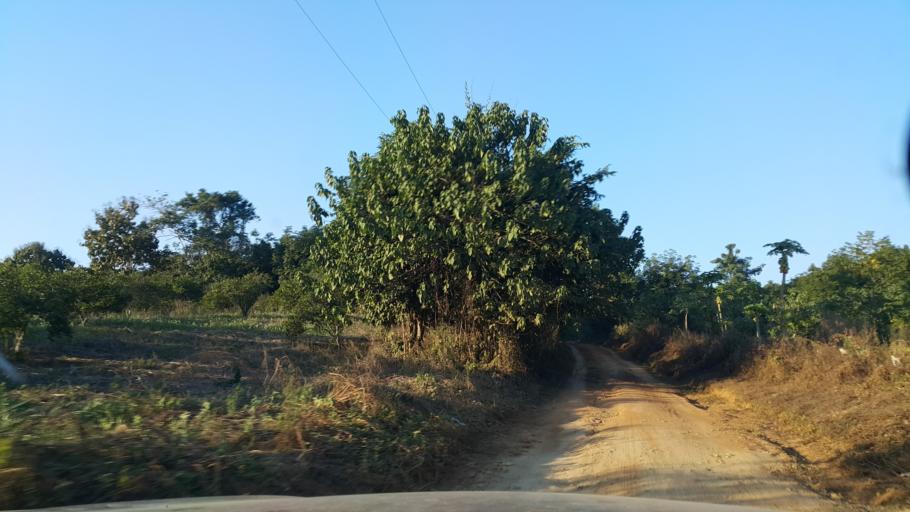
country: TH
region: Sukhothai
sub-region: Amphoe Si Satchanalai
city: Si Satchanalai
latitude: 17.5996
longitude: 99.6134
